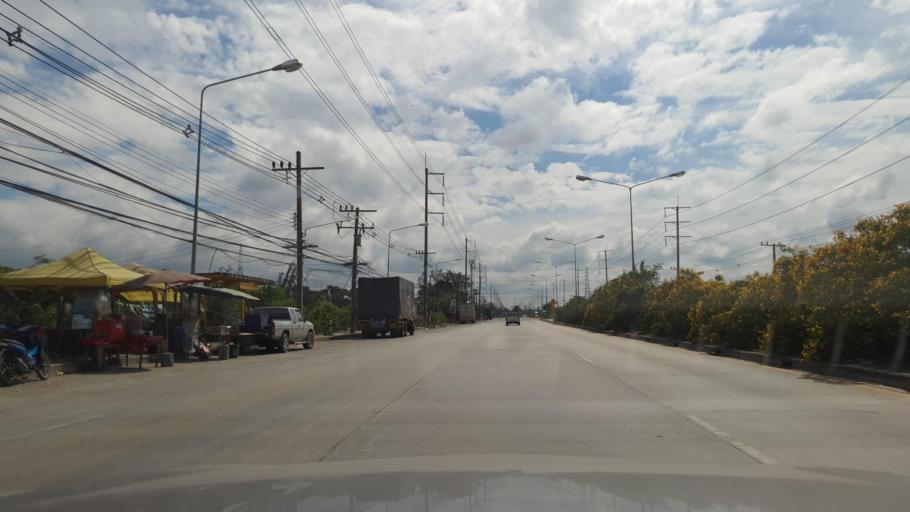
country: TH
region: Chachoengsao
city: Bang Pakong
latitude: 13.5303
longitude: 100.9923
